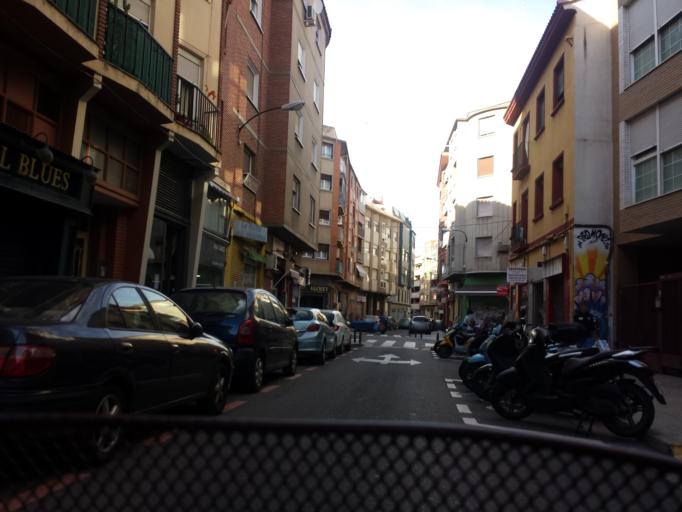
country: ES
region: Aragon
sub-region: Provincia de Zaragoza
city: Delicias
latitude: 41.6454
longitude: -0.8965
